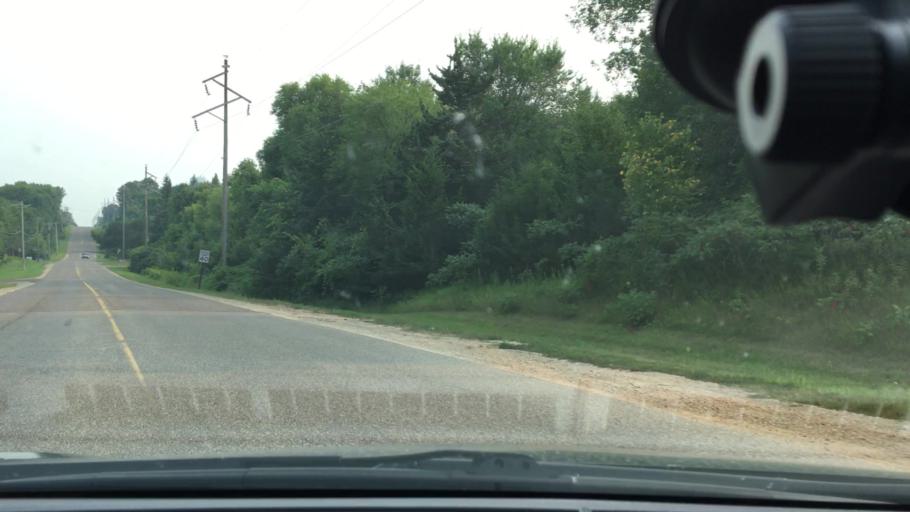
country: US
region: Minnesota
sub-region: Hennepin County
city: Champlin
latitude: 45.1990
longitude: -93.4425
